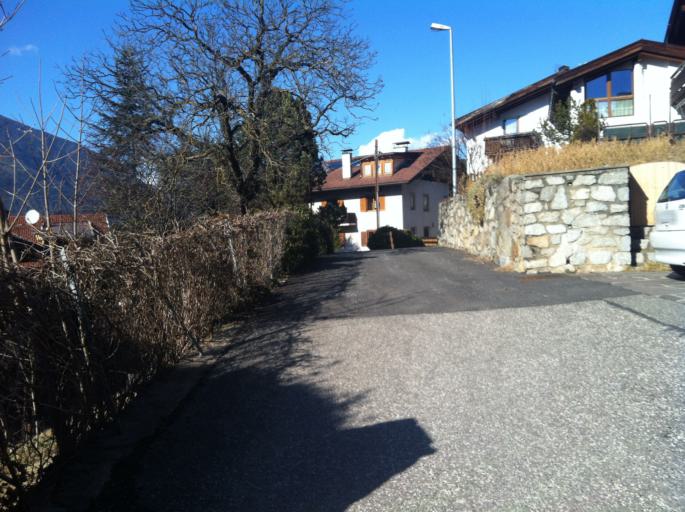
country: IT
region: Trentino-Alto Adige
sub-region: Bolzano
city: Bressanone
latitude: 46.7209
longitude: 11.6603
